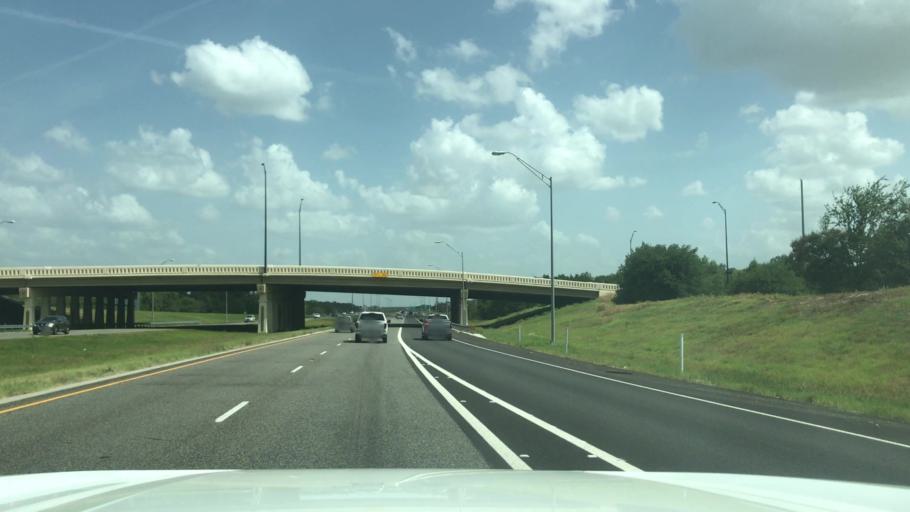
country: US
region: Texas
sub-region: Brazos County
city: Bryan
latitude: 30.6890
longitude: -96.3506
